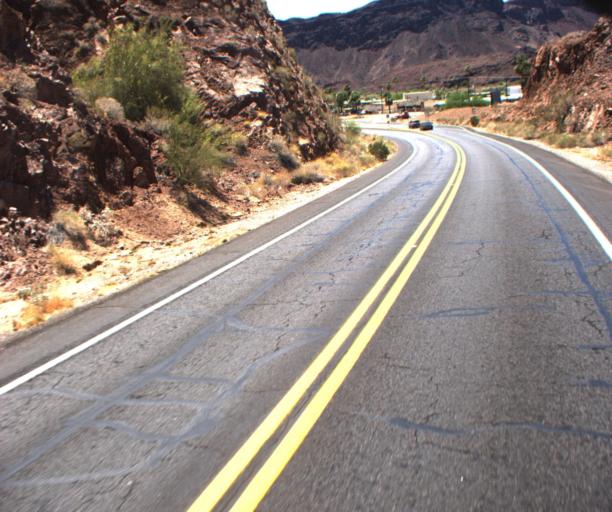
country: US
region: Arizona
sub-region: La Paz County
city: Cienega Springs
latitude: 34.2872
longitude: -114.1334
